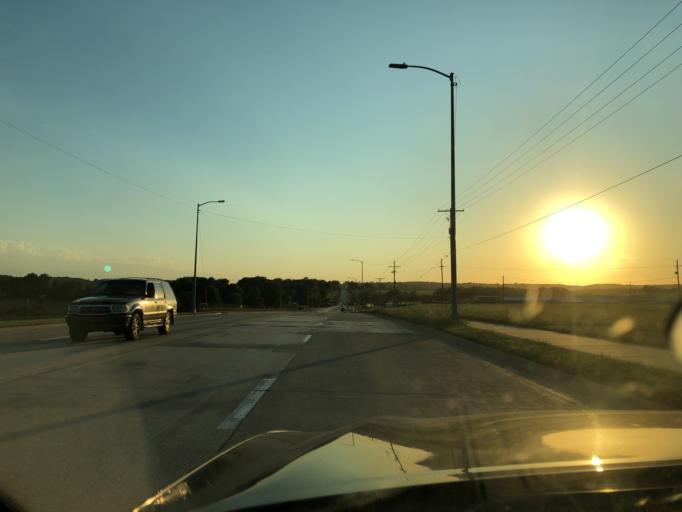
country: US
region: Kansas
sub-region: Leavenworth County
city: Lansing
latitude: 39.2667
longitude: -94.9342
